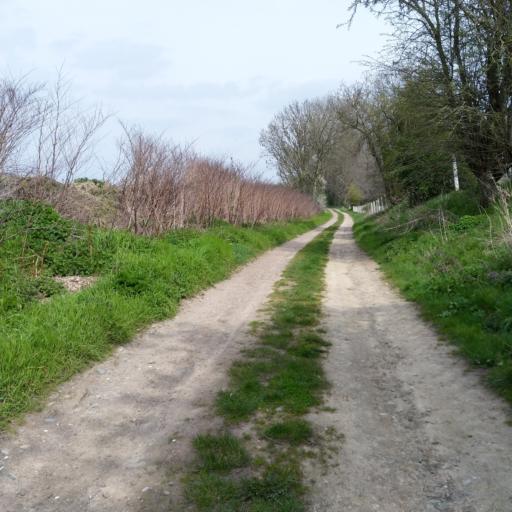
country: BE
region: Wallonia
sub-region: Province du Hainaut
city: Chasse Royale
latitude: 50.4047
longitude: 3.9310
